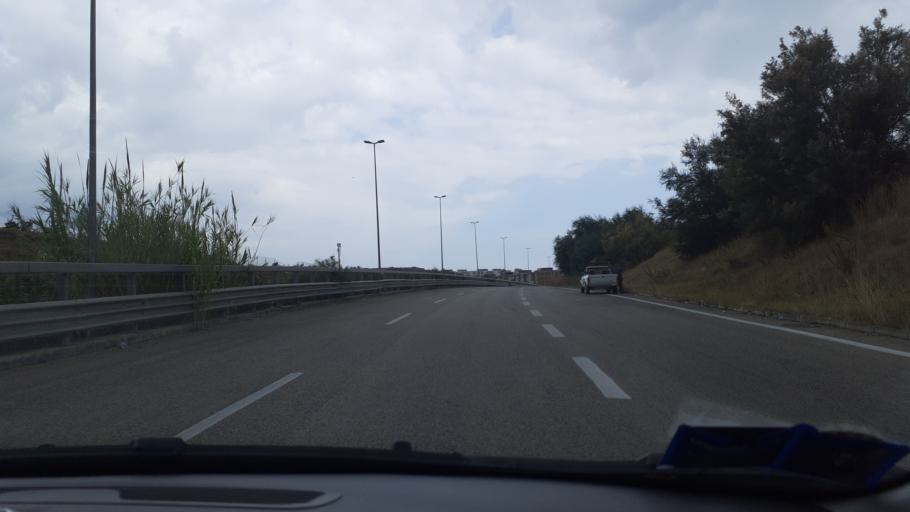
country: IT
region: Sicily
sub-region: Catania
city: Catania
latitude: 37.4758
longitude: 15.0426
